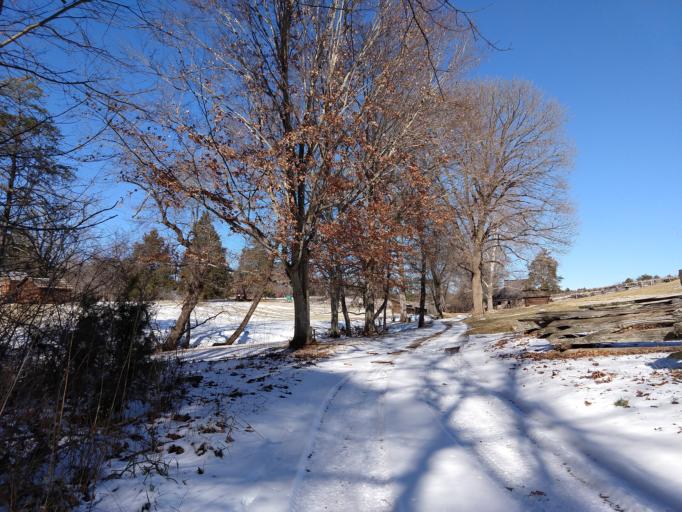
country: US
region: Virginia
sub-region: Franklin County
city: North Shore
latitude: 37.1176
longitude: -79.7301
